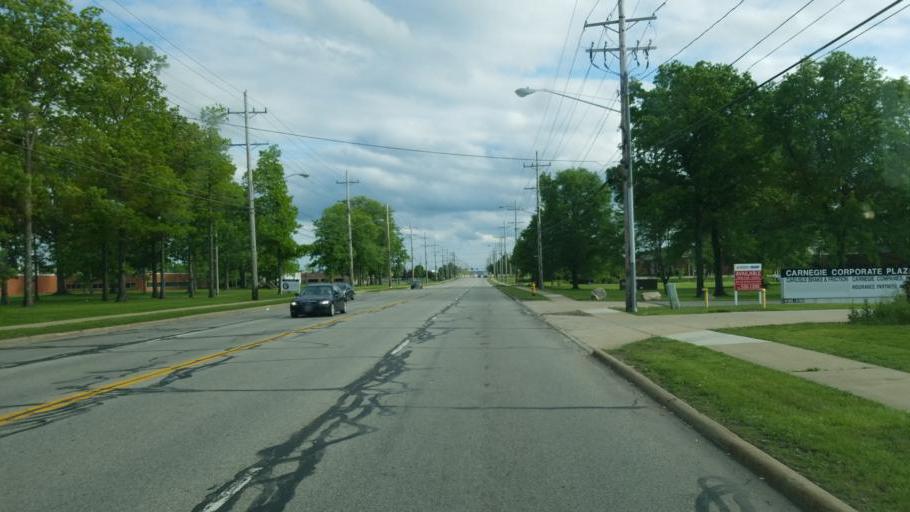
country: US
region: Ohio
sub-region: Cuyahoga County
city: Solon
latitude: 41.3918
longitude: -81.4691
